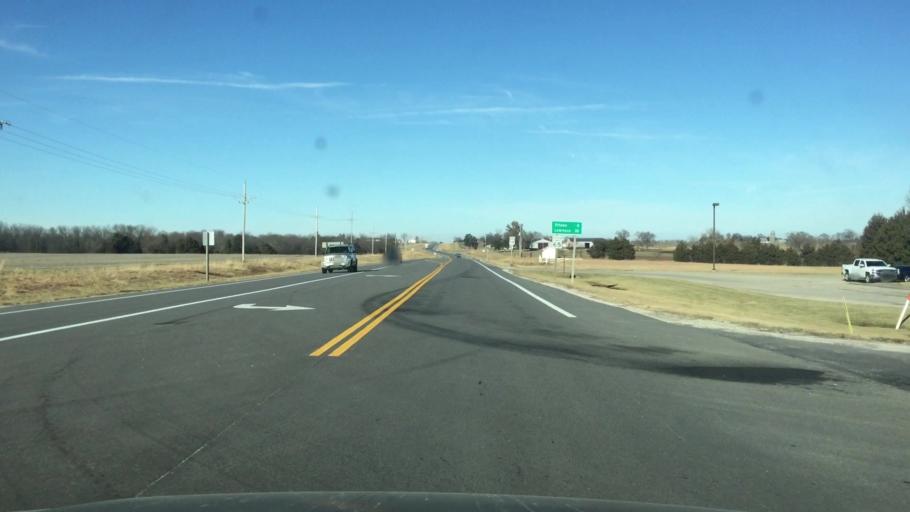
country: US
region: Kansas
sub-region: Franklin County
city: Ottawa
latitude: 38.4921
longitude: -95.2672
